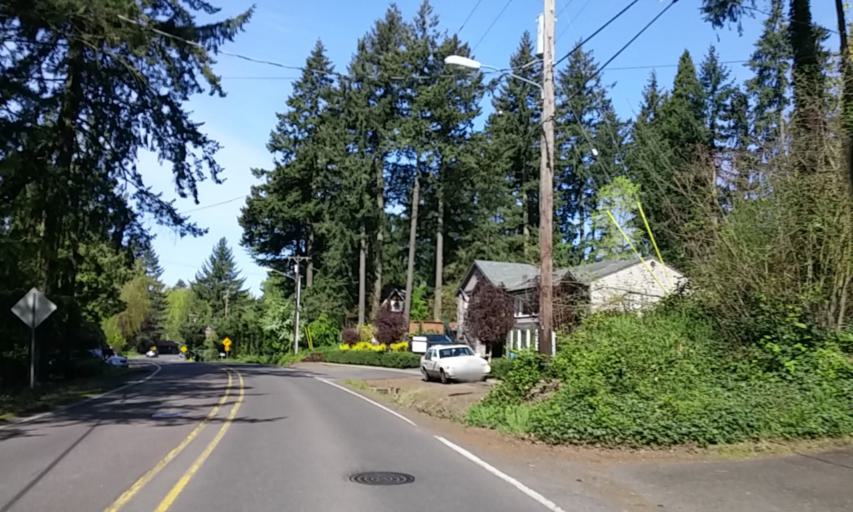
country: US
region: Oregon
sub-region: Washington County
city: Cedar Hills
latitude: 45.4965
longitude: -122.7835
